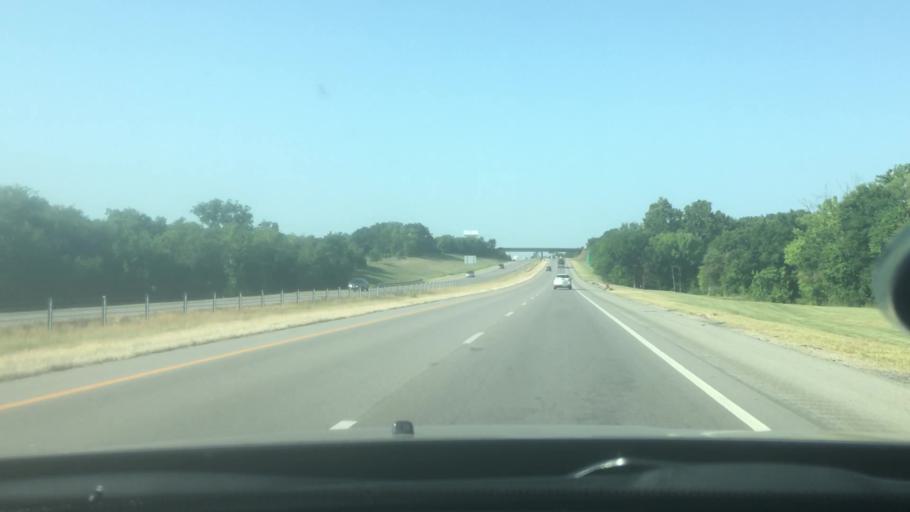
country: US
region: Oklahoma
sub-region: Bryan County
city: Durant
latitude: 33.9877
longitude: -96.4112
